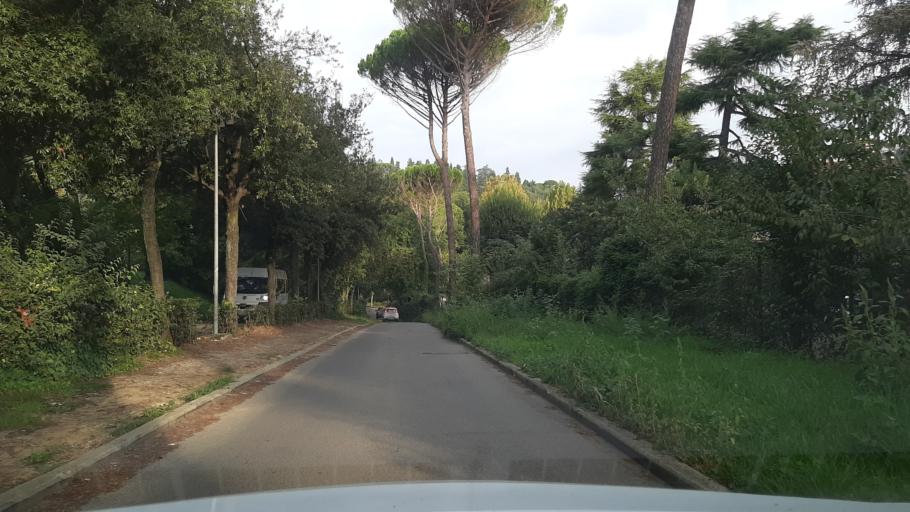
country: IT
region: Tuscany
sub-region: Province of Florence
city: Florence
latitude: 43.7571
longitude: 11.2723
